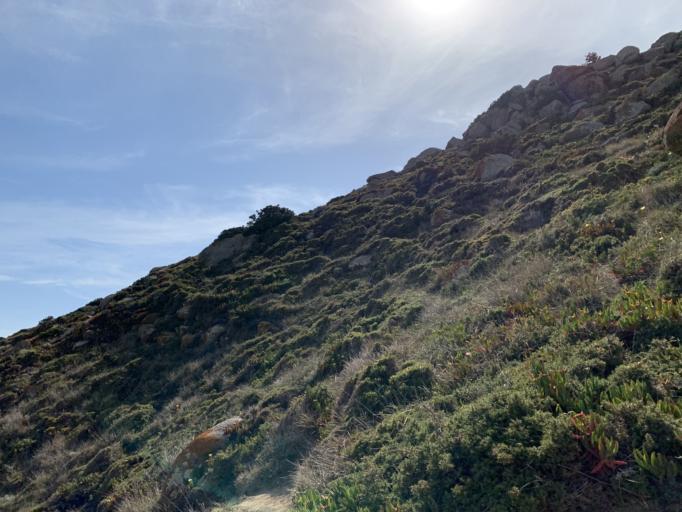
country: PT
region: Lisbon
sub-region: Sintra
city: Colares
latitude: 38.7778
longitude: -9.4972
